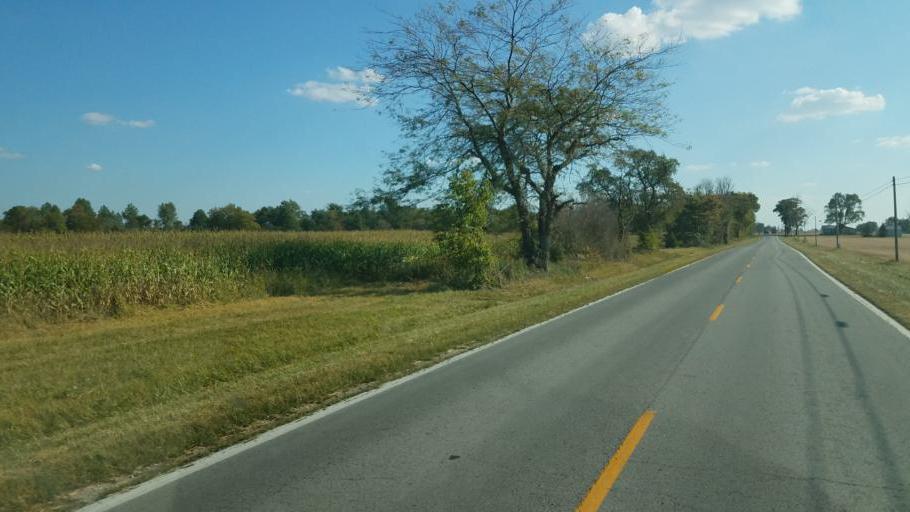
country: US
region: Ohio
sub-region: Hardin County
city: Forest
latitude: 40.6310
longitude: -83.3806
